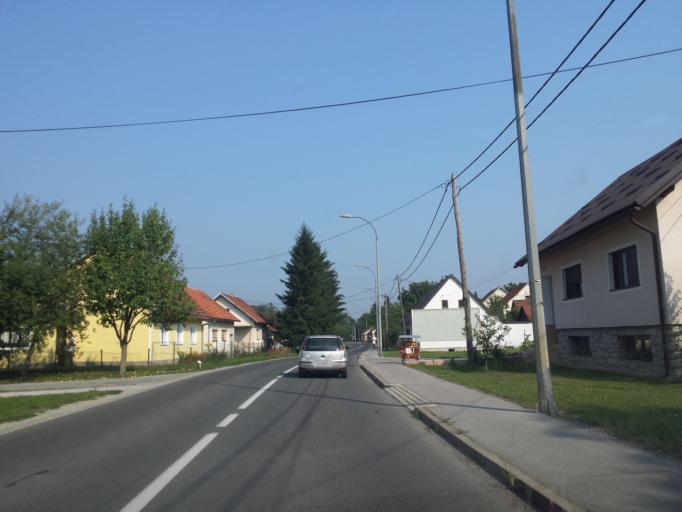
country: HR
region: Karlovacka
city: Ostarije
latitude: 45.2340
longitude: 15.2564
